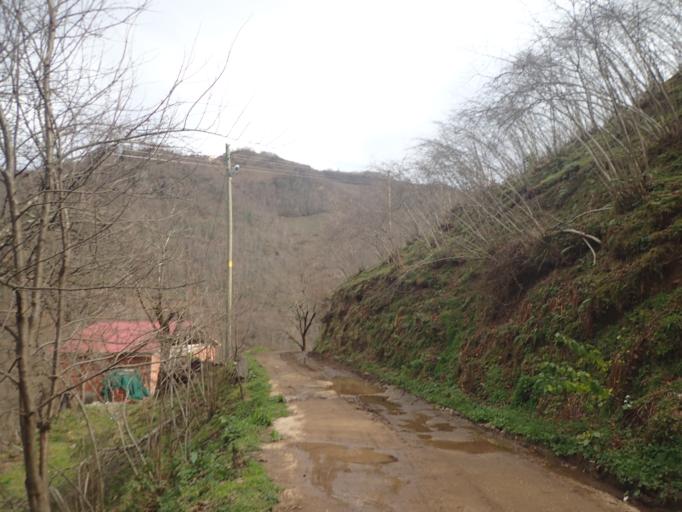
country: TR
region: Ordu
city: Camas
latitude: 40.8953
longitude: 37.5799
